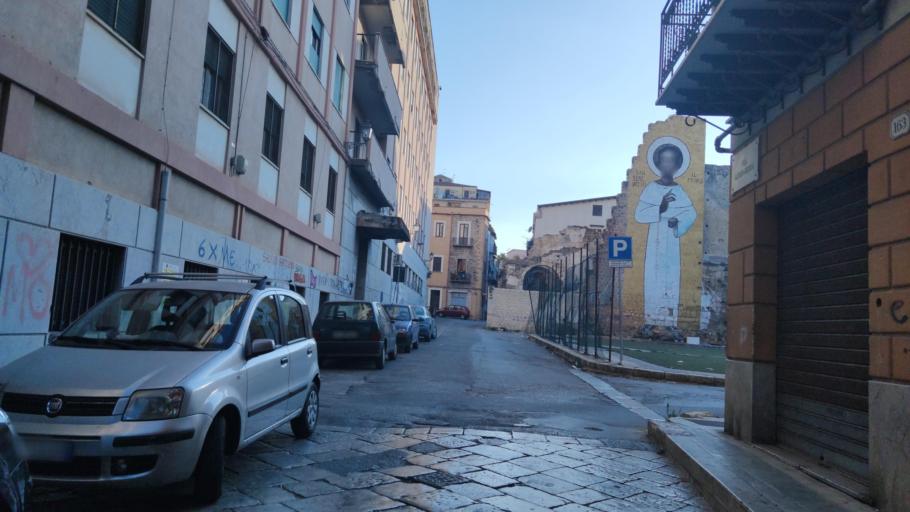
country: IT
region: Sicily
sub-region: Palermo
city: Palermo
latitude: 38.1100
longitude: 13.3581
